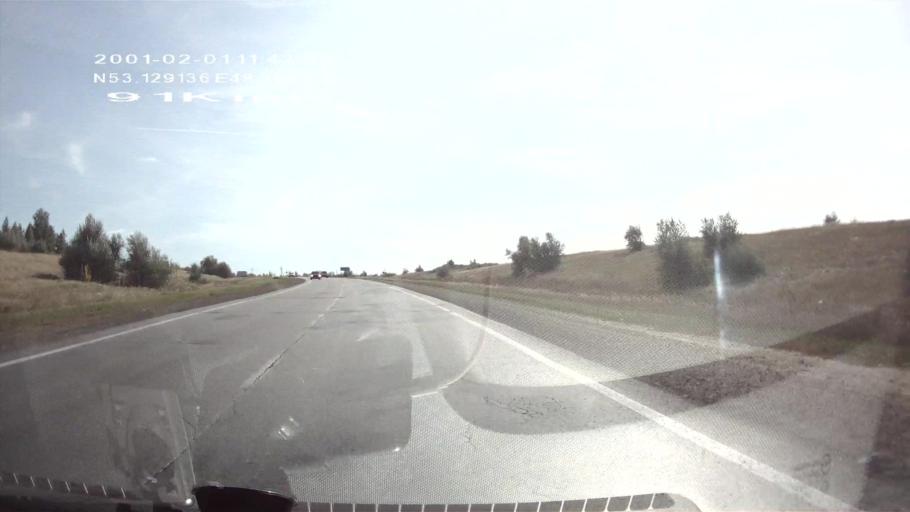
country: RU
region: Samara
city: Varlamovo
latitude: 53.1280
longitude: 48.2891
